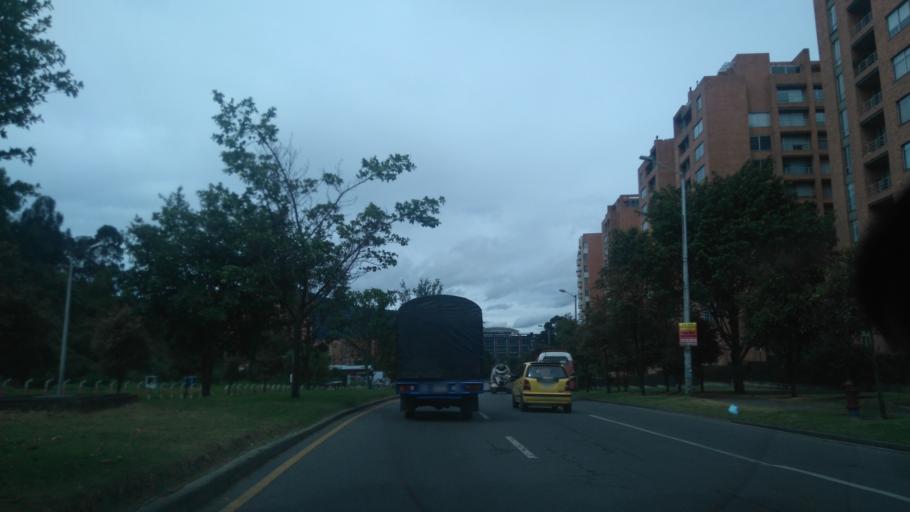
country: CO
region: Bogota D.C.
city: Barrio San Luis
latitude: 4.7150
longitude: -74.0288
